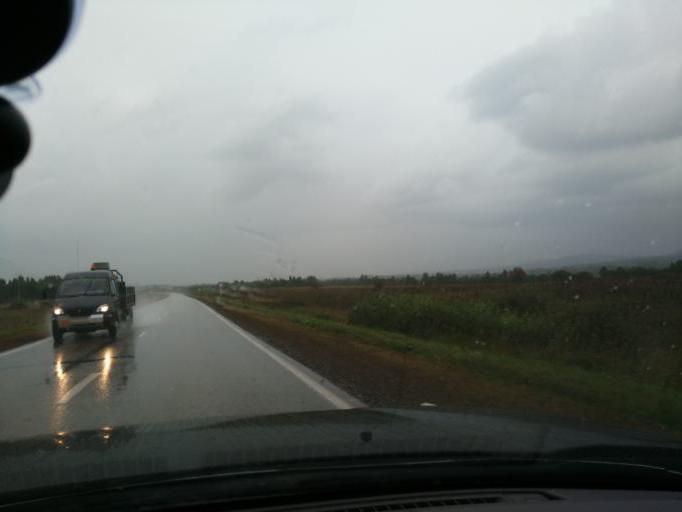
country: RU
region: Perm
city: Barda
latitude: 57.0767
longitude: 55.5426
